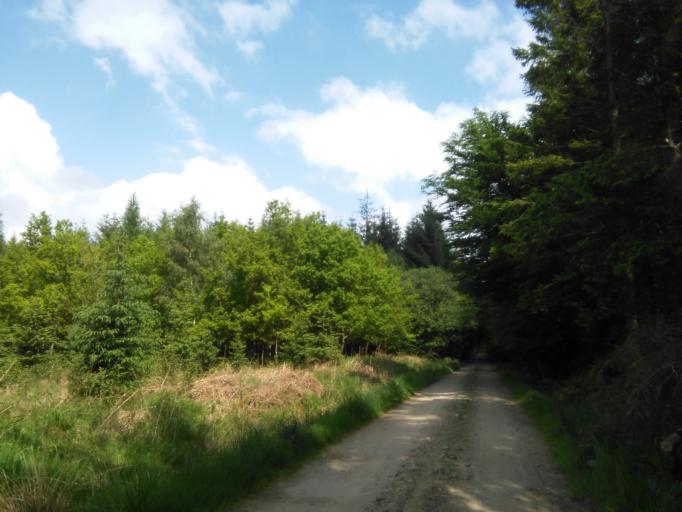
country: DK
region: Central Jutland
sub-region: Favrskov Kommune
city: Hammel
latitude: 56.2631
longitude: 9.9361
